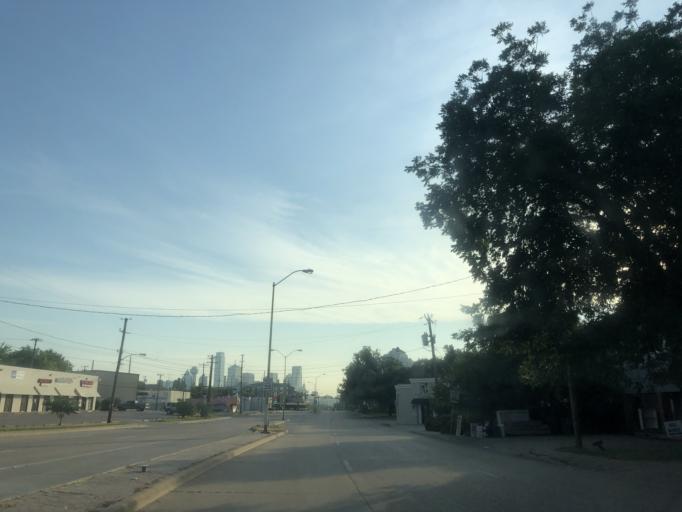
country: US
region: Texas
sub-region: Dallas County
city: Dallas
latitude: 32.7566
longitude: -96.8227
